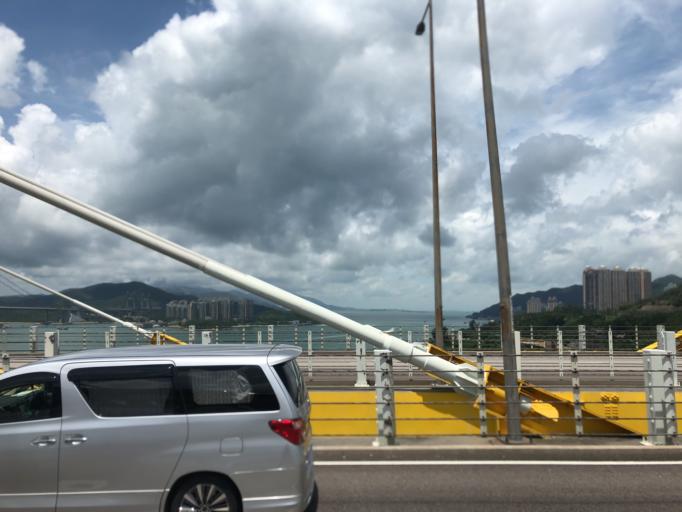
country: HK
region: Tsuen Wan
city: Tsuen Wan
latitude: 22.3664
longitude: 114.0786
